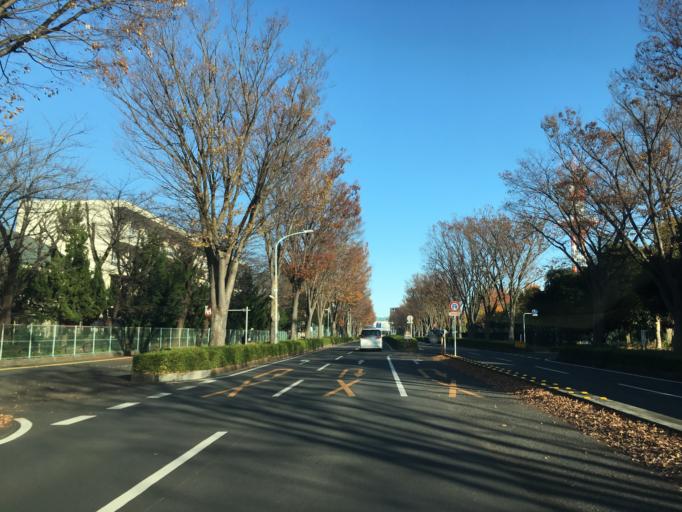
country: JP
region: Saitama
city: Tokorozawa
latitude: 35.8015
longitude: 139.4754
